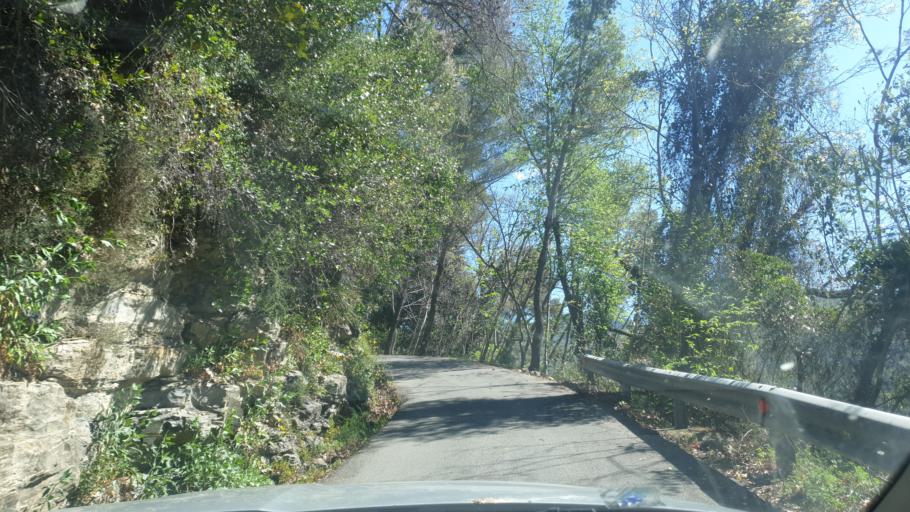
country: IT
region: Liguria
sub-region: Provincia di Genova
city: Avegno
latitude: 44.3785
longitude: 9.1431
